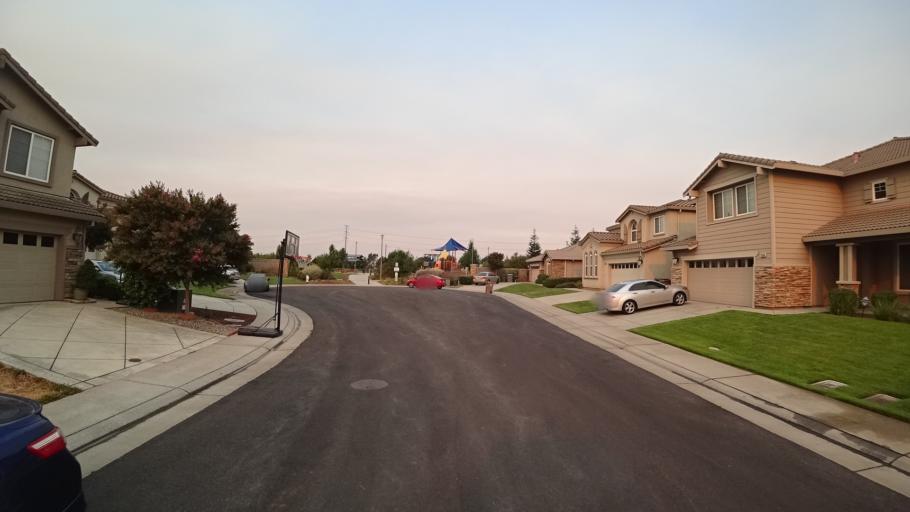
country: US
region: California
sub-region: Sacramento County
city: Laguna
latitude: 38.3832
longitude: -121.4481
